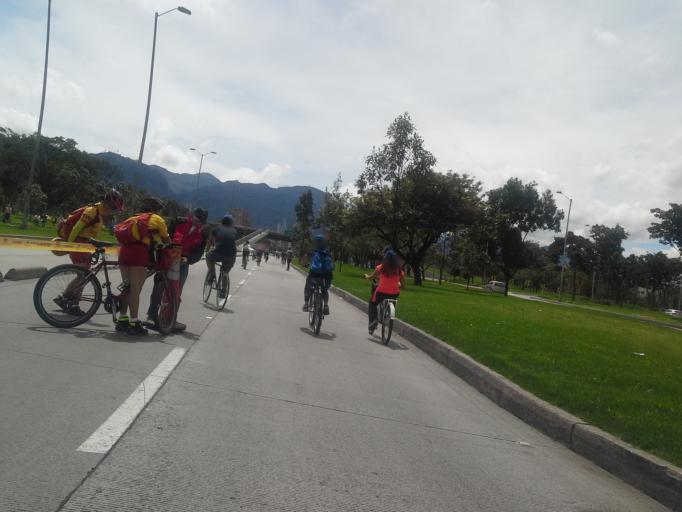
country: CO
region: Bogota D.C.
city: Bogota
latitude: 4.6418
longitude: -74.0960
